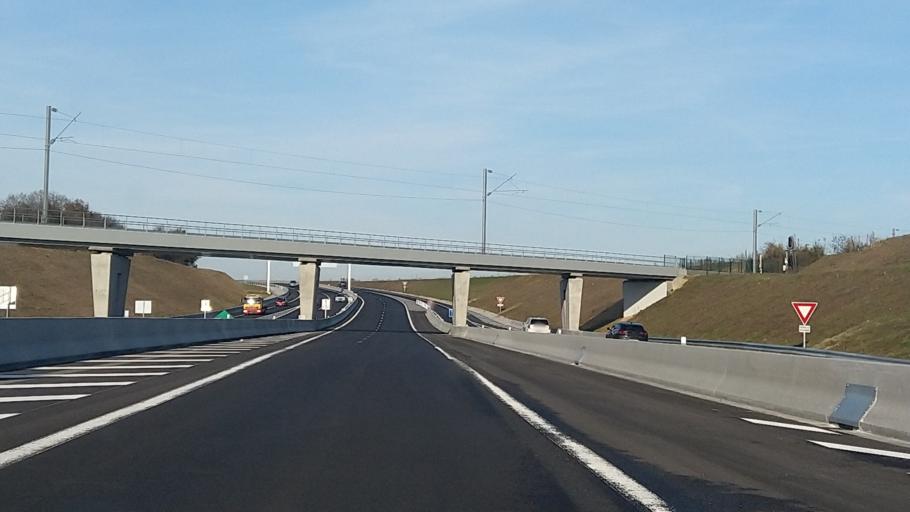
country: FR
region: Ile-de-France
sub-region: Departement du Val-d'Oise
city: Montsoult
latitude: 49.0692
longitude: 2.3310
